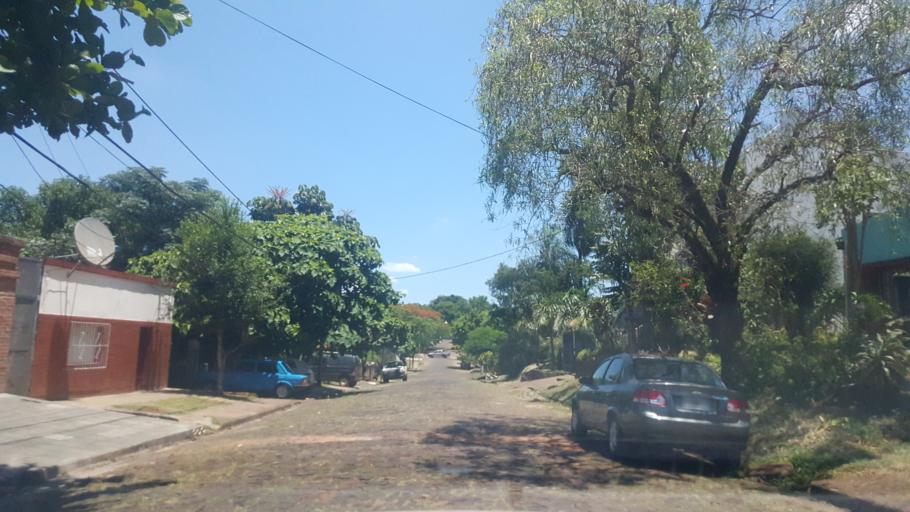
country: AR
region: Misiones
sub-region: Departamento de Capital
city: Posadas
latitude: -27.3607
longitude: -55.9056
